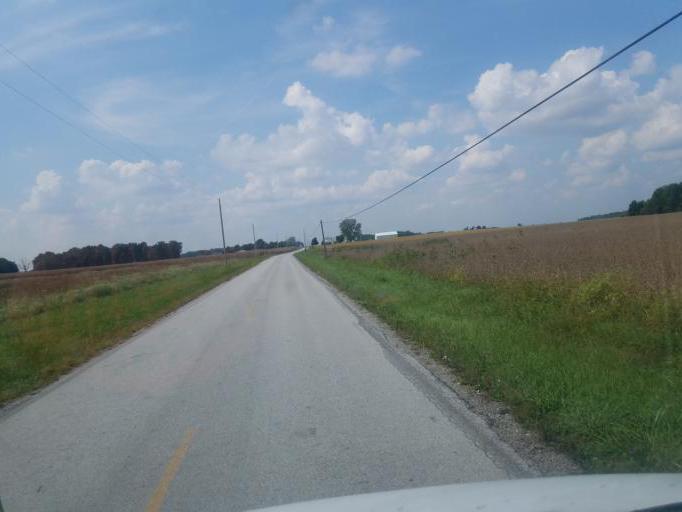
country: US
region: Ohio
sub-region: Hardin County
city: Kenton
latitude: 40.6427
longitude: -83.6664
